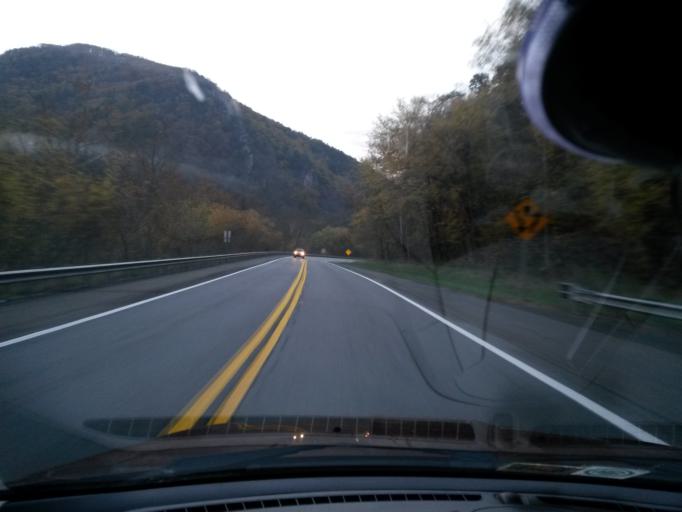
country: US
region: Virginia
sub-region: Botetourt County
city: Fincastle
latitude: 37.6448
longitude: -79.8126
